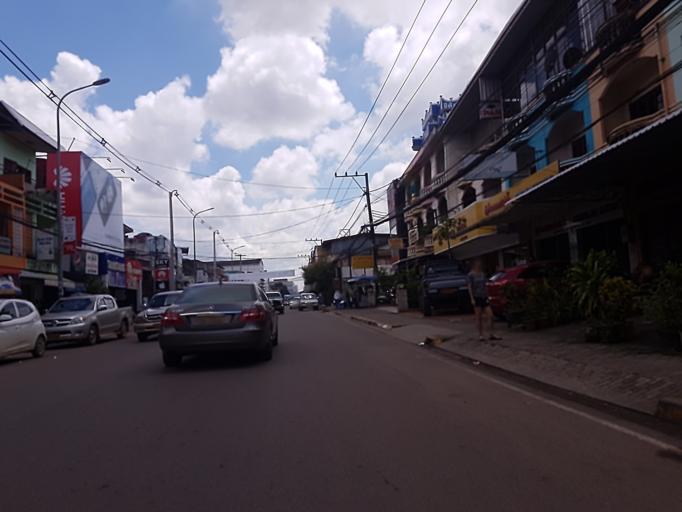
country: LA
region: Vientiane
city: Vientiane
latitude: 17.9620
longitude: 102.6220
